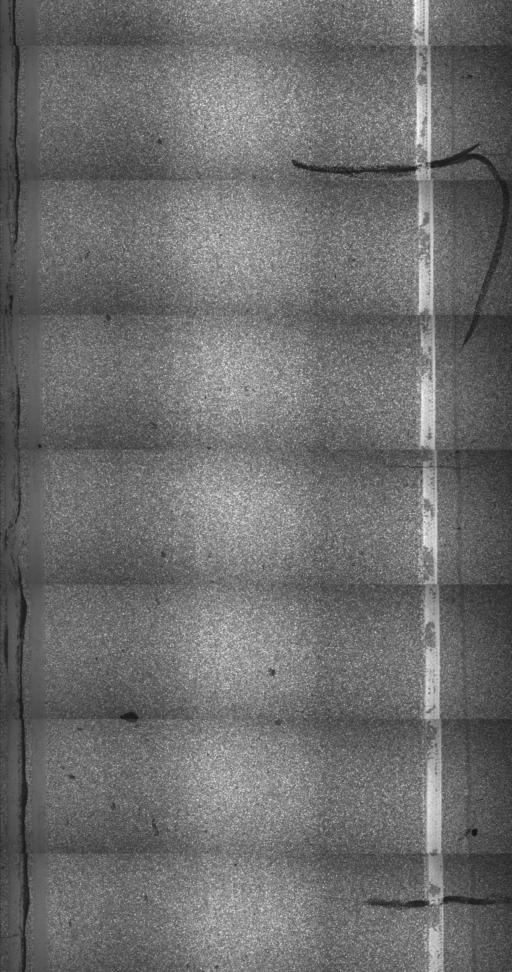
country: US
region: Vermont
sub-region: Franklin County
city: Swanton
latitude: 44.9088
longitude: -73.1016
